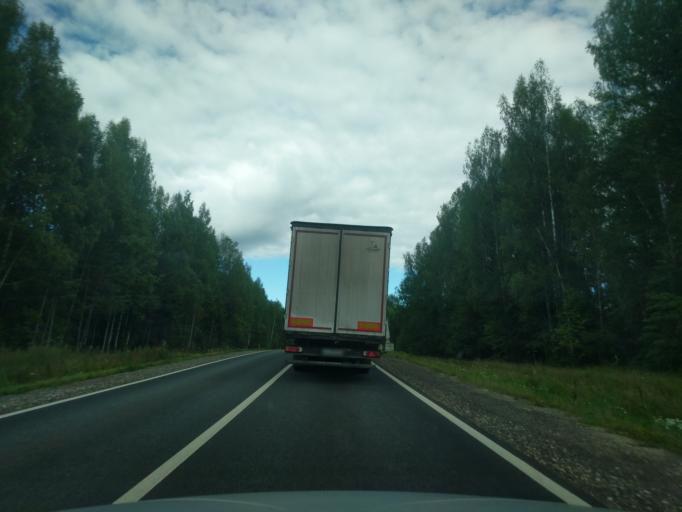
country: RU
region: Kostroma
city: Kadyy
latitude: 57.8476
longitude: 43.4694
